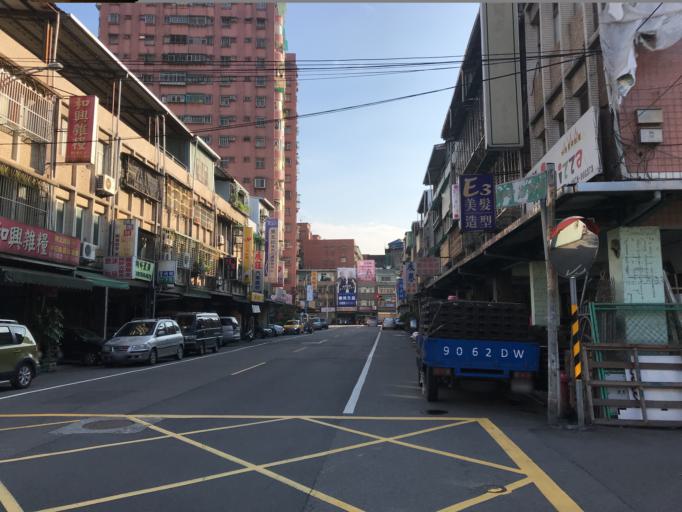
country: TW
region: Taiwan
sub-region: Taoyuan
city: Taoyuan
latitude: 24.9282
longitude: 121.3712
